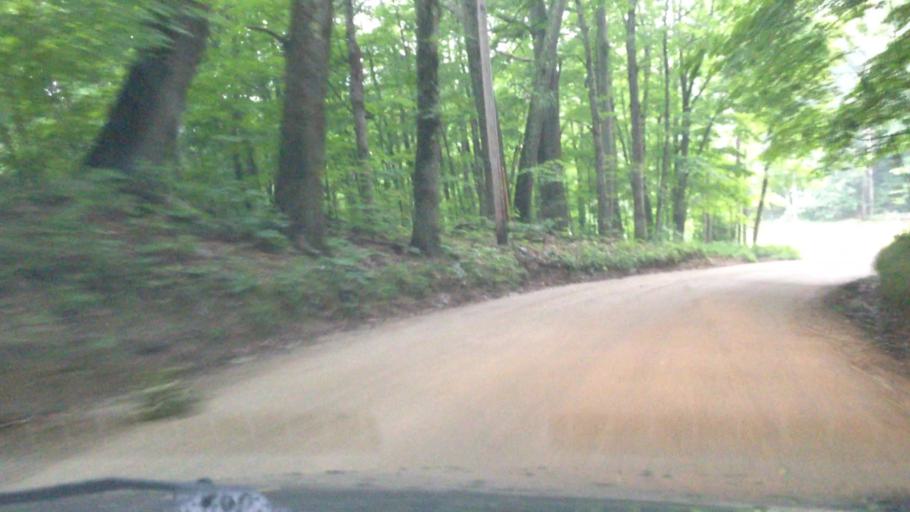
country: US
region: New Hampshire
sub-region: Cheshire County
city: Marlborough
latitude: 42.8949
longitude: -72.1593
